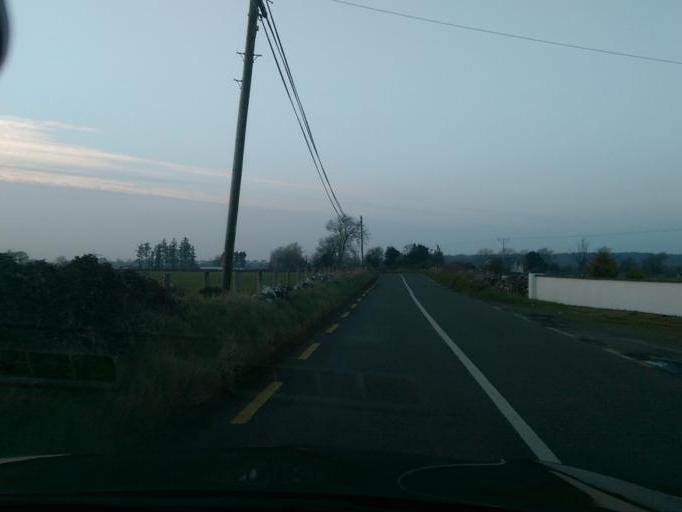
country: IE
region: Connaught
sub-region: County Galway
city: Loughrea
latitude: 53.2203
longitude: -8.6232
